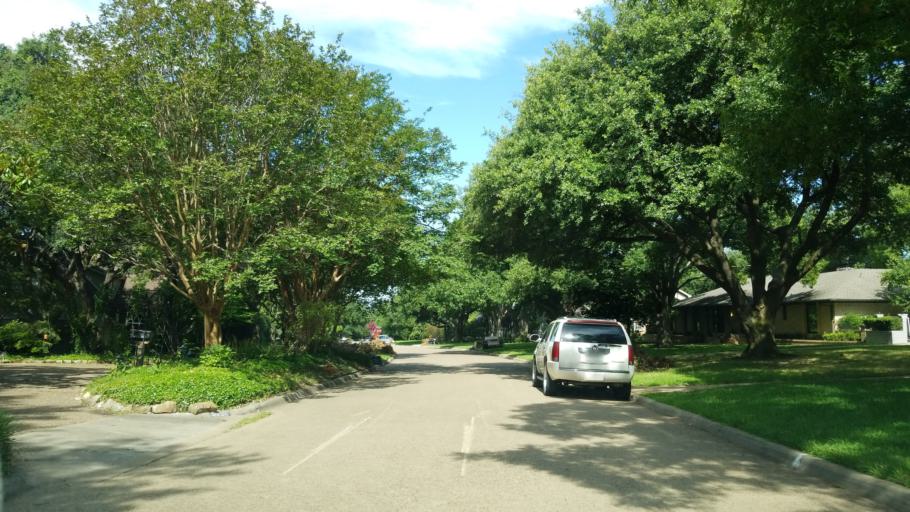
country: US
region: Texas
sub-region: Dallas County
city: Addison
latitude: 32.9072
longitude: -96.8365
